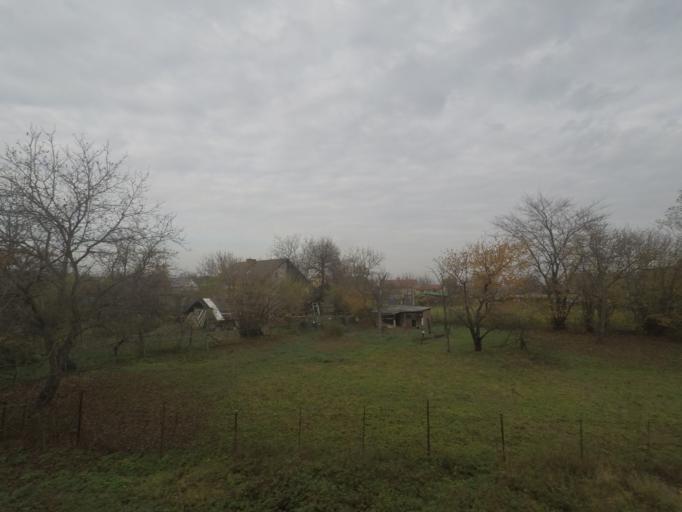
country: PL
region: Subcarpathian Voivodeship
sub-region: Przemysl
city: Przemysl
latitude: 49.7848
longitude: 22.7993
